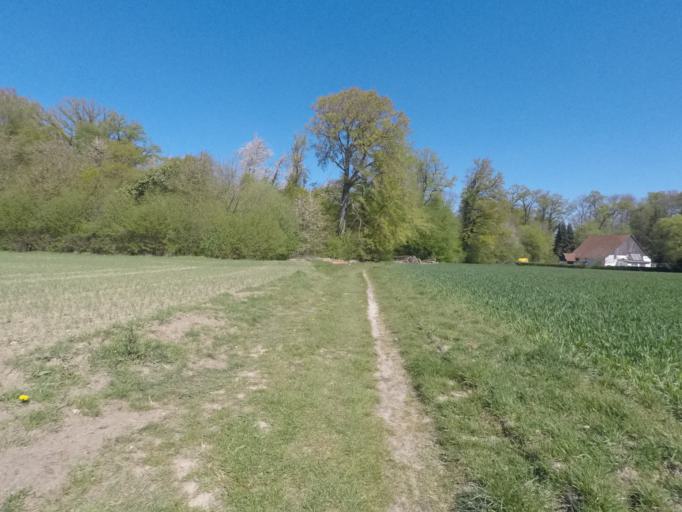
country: DE
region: North Rhine-Westphalia
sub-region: Regierungsbezirk Detmold
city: Bielefeld
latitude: 52.0082
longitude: 8.5807
